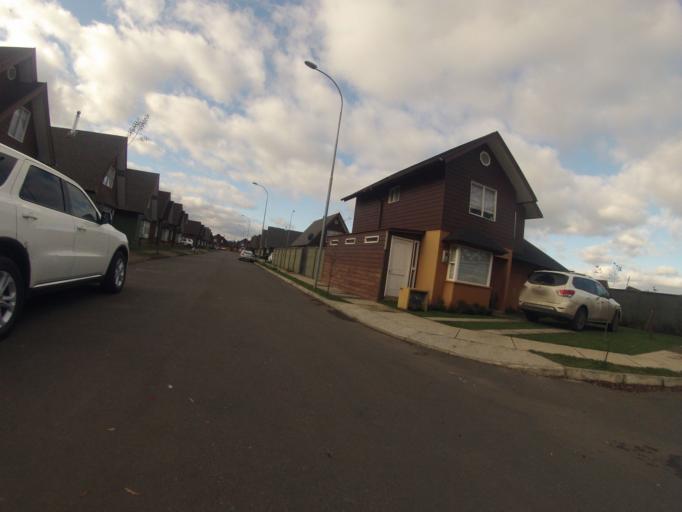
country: CL
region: Araucania
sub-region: Provincia de Cautin
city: Temuco
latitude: -38.7426
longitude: -72.6464
